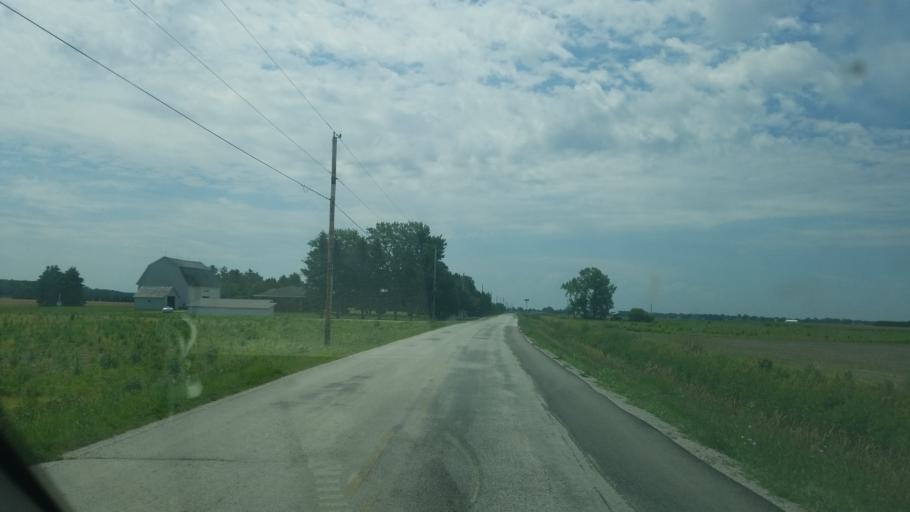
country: US
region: Ohio
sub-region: Wood County
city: Bowling Green
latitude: 41.2903
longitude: -83.5926
